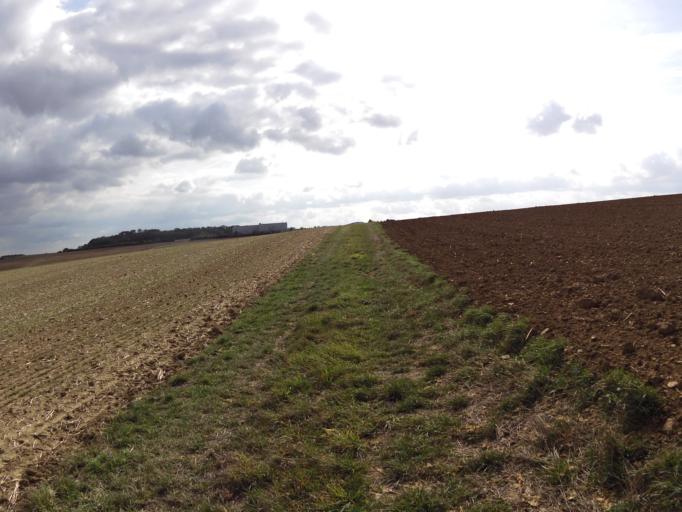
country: DE
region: Bavaria
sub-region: Regierungsbezirk Unterfranken
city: Reichenberg
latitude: 49.7009
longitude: 9.9421
